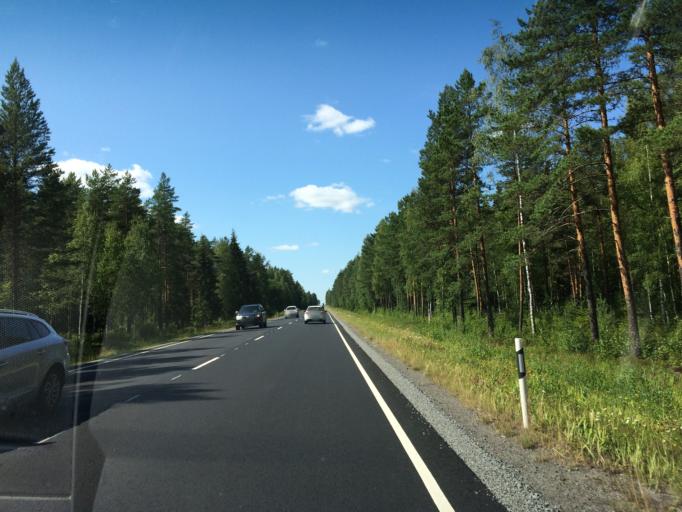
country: FI
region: Pirkanmaa
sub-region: Lounais-Pirkanmaa
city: Kiikoinen
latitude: 61.4734
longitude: 22.5039
